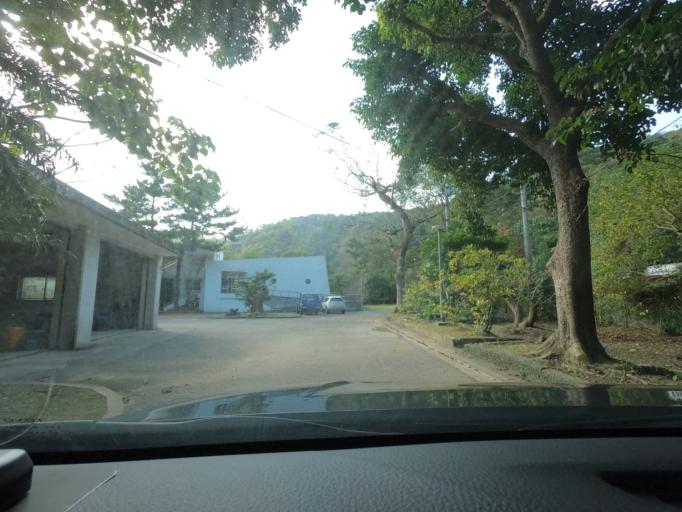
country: JP
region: Okinawa
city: Nago
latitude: 26.7633
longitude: 128.2157
